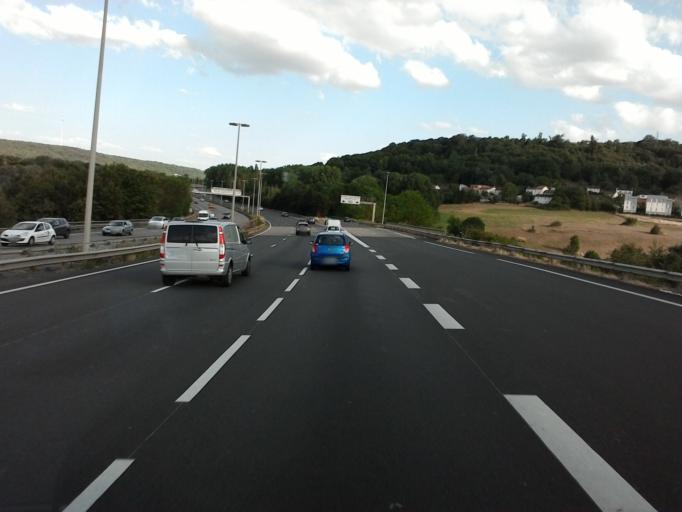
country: FR
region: Lorraine
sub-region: Departement de Meurthe-et-Moselle
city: Champigneulles
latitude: 48.7305
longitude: 6.1600
